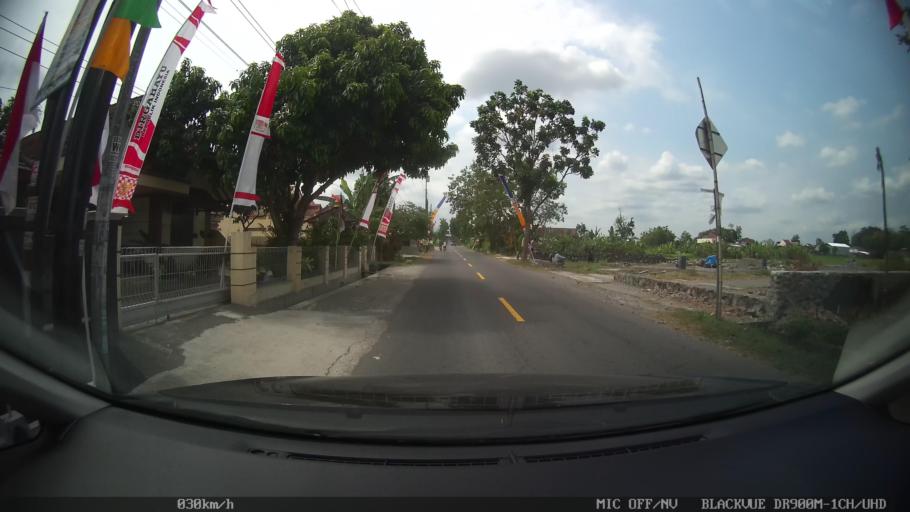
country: ID
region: Central Java
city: Candi Prambanan
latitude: -7.7544
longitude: 110.4807
